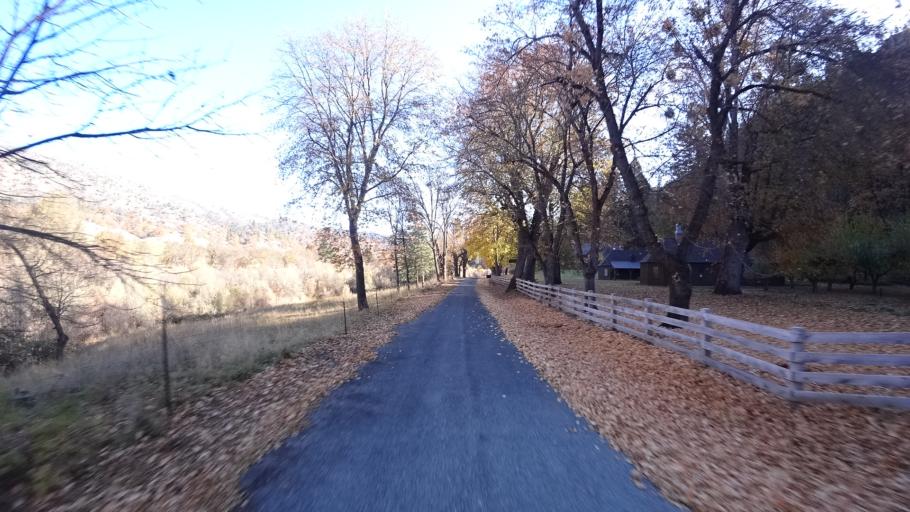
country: US
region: California
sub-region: Siskiyou County
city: Yreka
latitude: 41.8371
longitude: -122.9395
